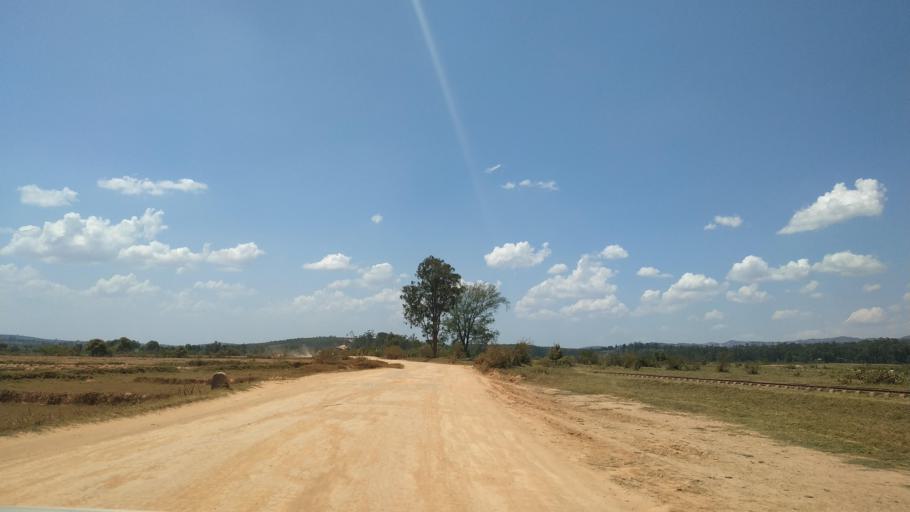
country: MG
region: Alaotra Mangoro
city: Ambatondrazaka
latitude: -18.1917
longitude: 48.2575
